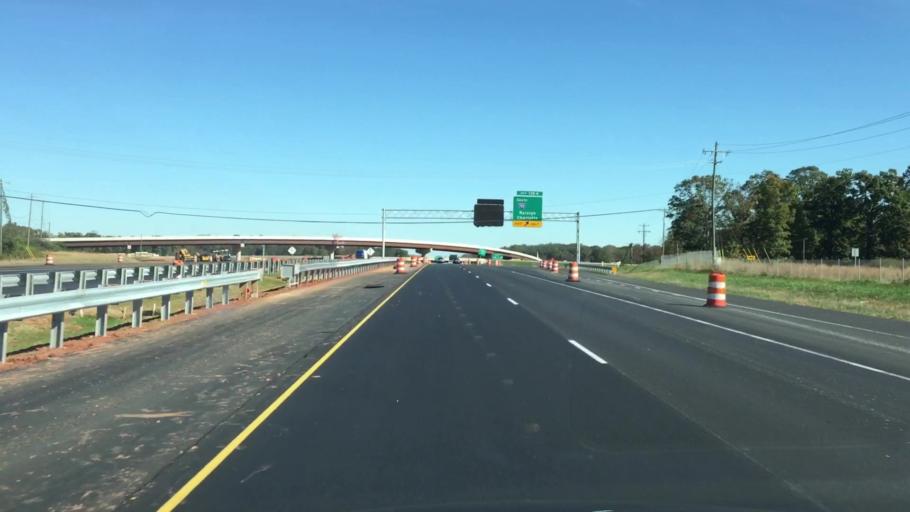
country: US
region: North Carolina
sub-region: Guilford County
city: Greensboro
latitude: 36.1388
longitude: -79.7383
